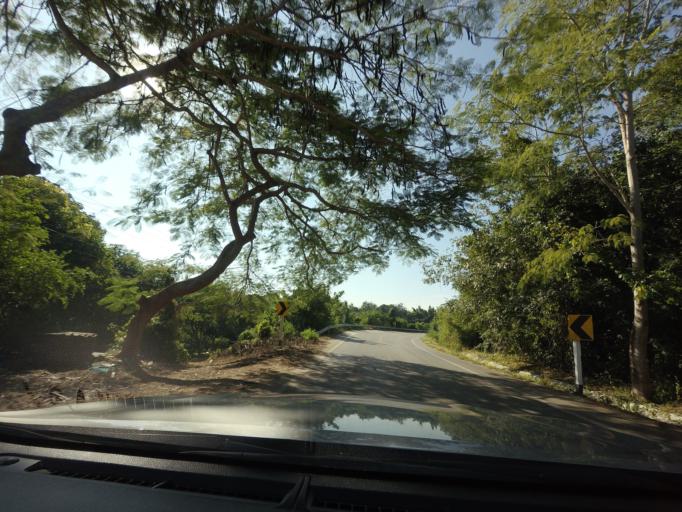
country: TH
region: Phrae
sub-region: Amphoe Wang Chin
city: Wang Chin
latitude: 17.7162
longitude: 99.6767
